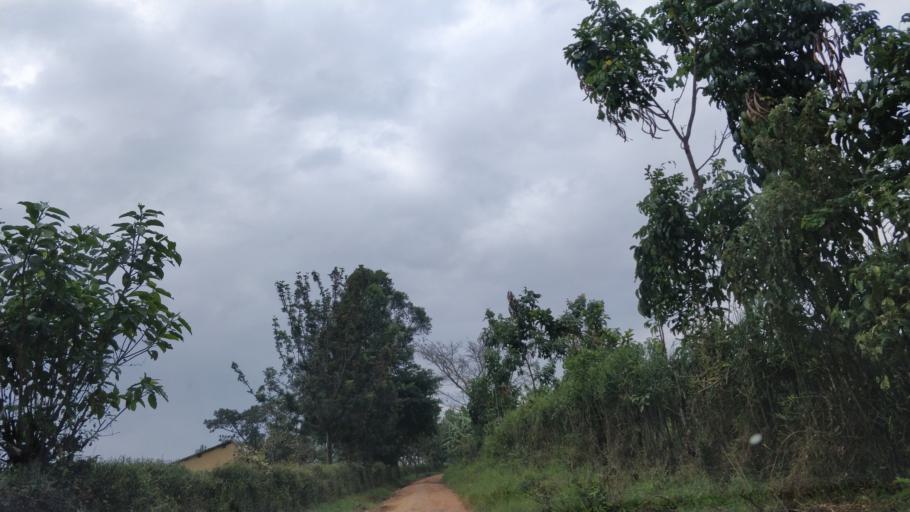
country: UG
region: Western Region
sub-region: Sheema District
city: Kibingo
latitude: -0.6439
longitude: 30.4954
